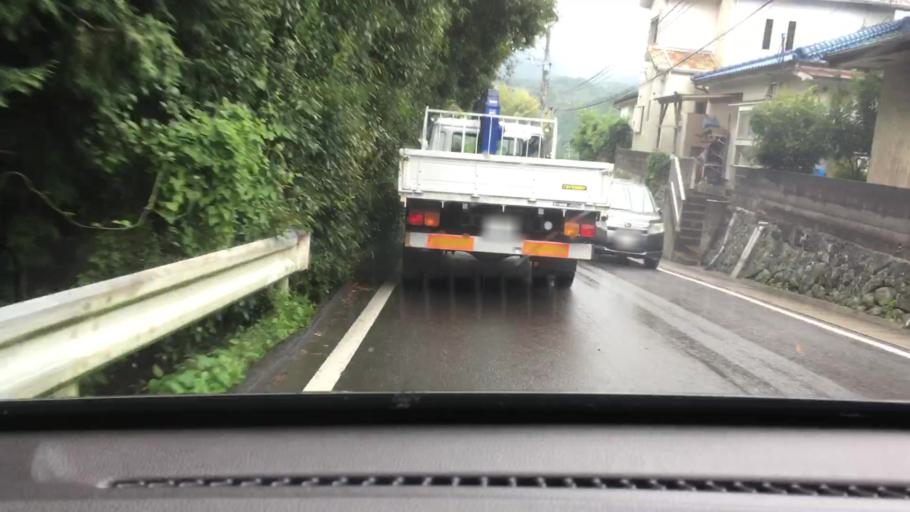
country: JP
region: Nagasaki
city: Togitsu
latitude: 32.8572
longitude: 129.7787
